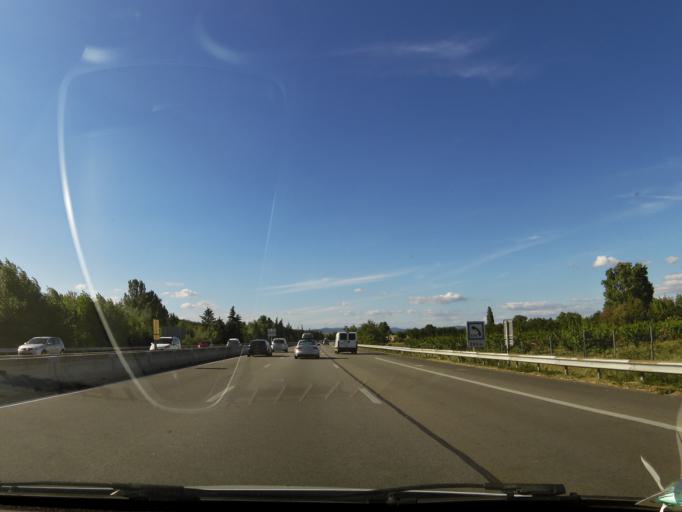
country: FR
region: Rhone-Alpes
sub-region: Departement de la Drome
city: Saulce-sur-Rhone
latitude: 44.6904
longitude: 4.7915
